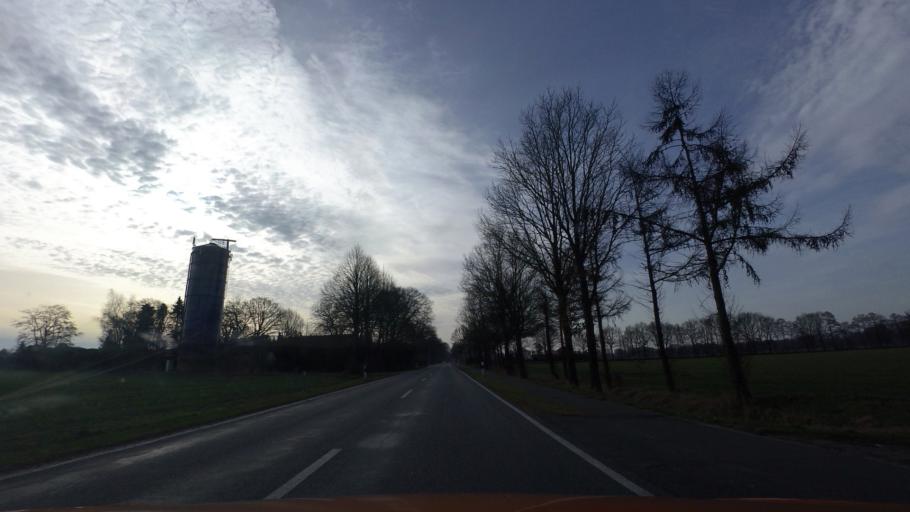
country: DE
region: Lower Saxony
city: Oldenburg
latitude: 53.0996
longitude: 8.2832
